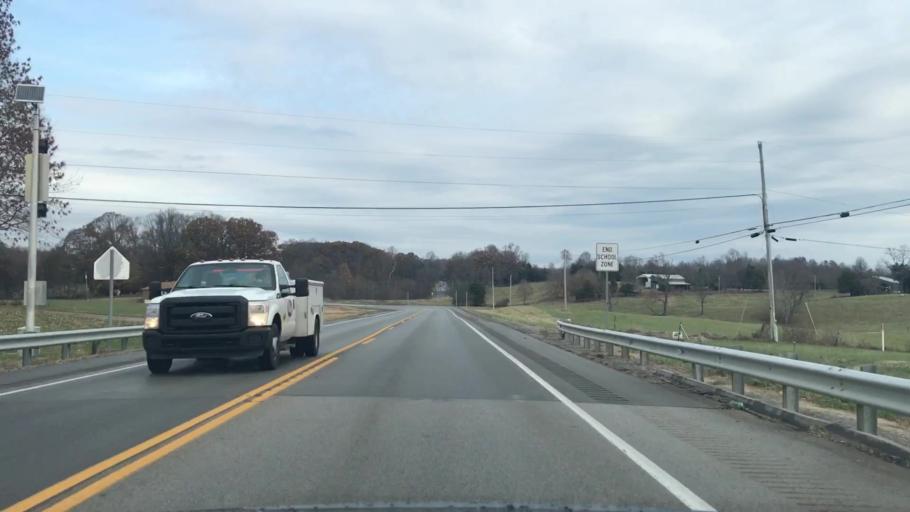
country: US
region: Kentucky
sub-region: Monroe County
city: Tompkinsville
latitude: 36.7590
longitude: -85.6871
